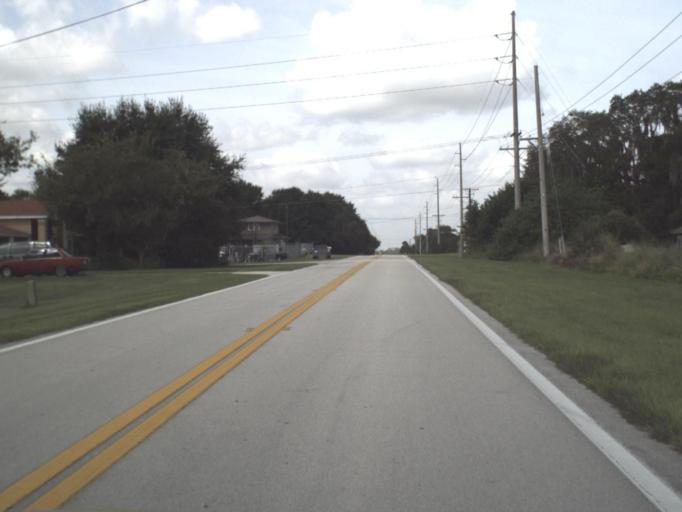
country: US
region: Florida
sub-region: Polk County
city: Jan-Phyl Village
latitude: 28.0040
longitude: -81.7545
